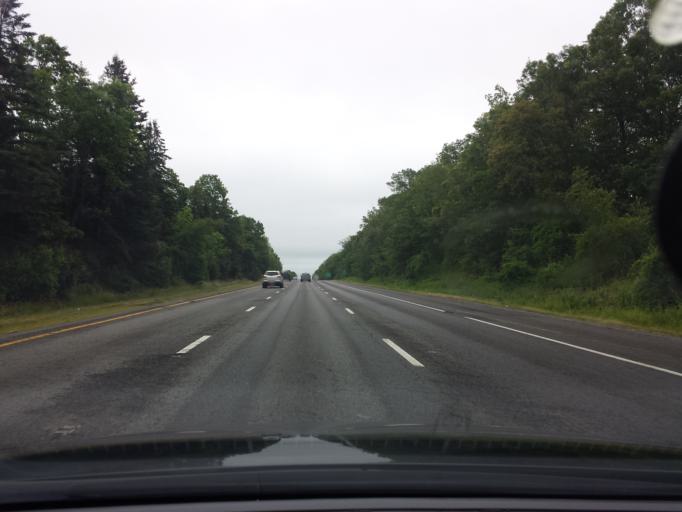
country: US
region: Massachusetts
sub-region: Bristol County
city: Seekonk
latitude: 41.7992
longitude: -71.3247
